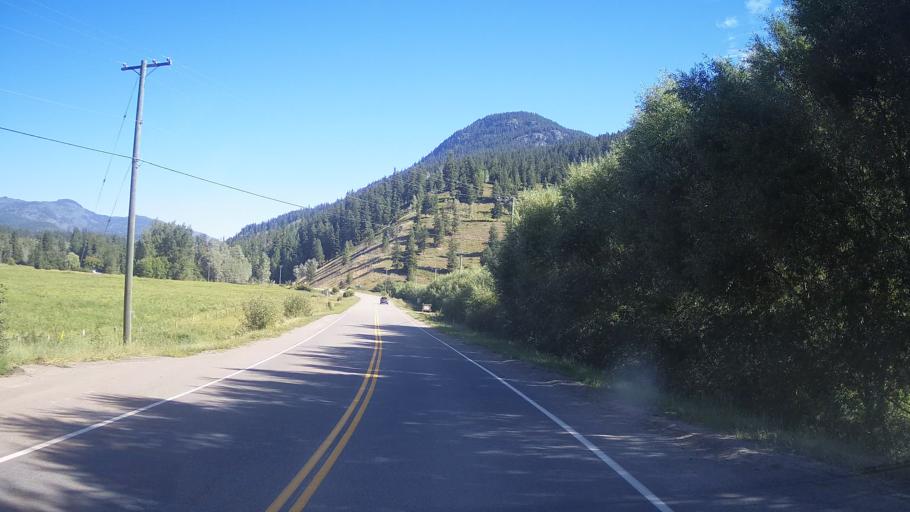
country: CA
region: British Columbia
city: Kamloops
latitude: 51.4327
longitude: -120.2078
